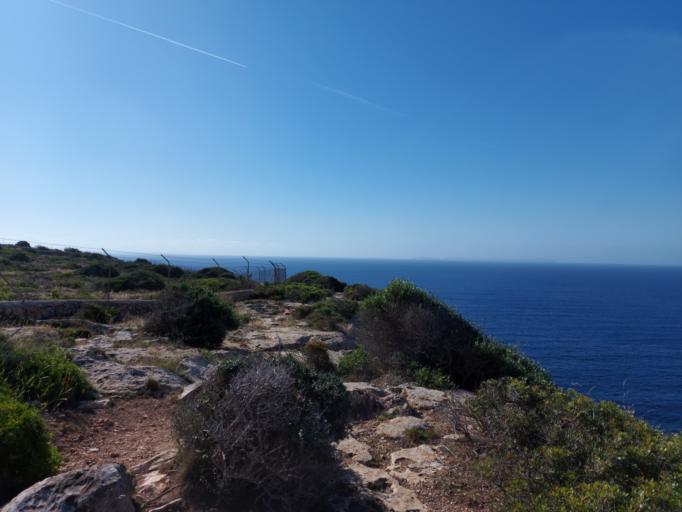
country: ES
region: Balearic Islands
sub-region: Illes Balears
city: s'Arenal
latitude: 39.3632
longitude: 2.7882
